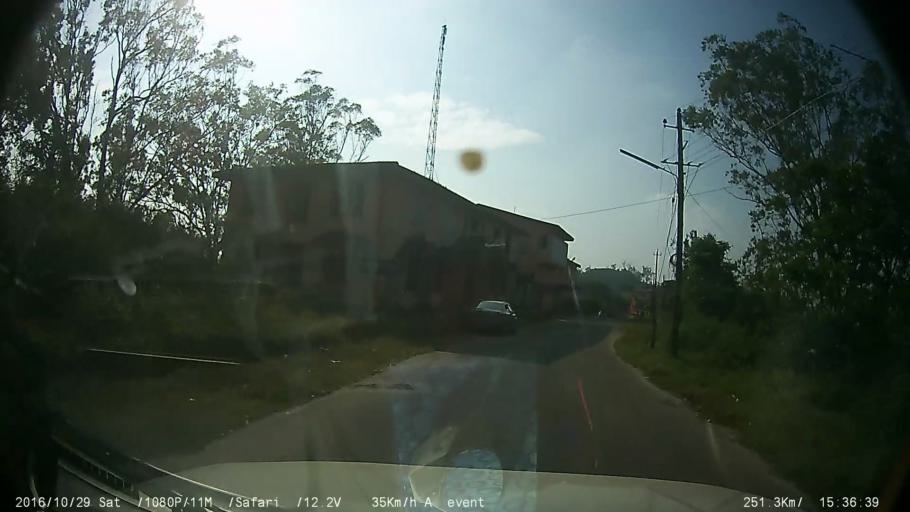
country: IN
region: Karnataka
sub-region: Kodagu
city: Madikeri
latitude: 12.4170
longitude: 75.7339
